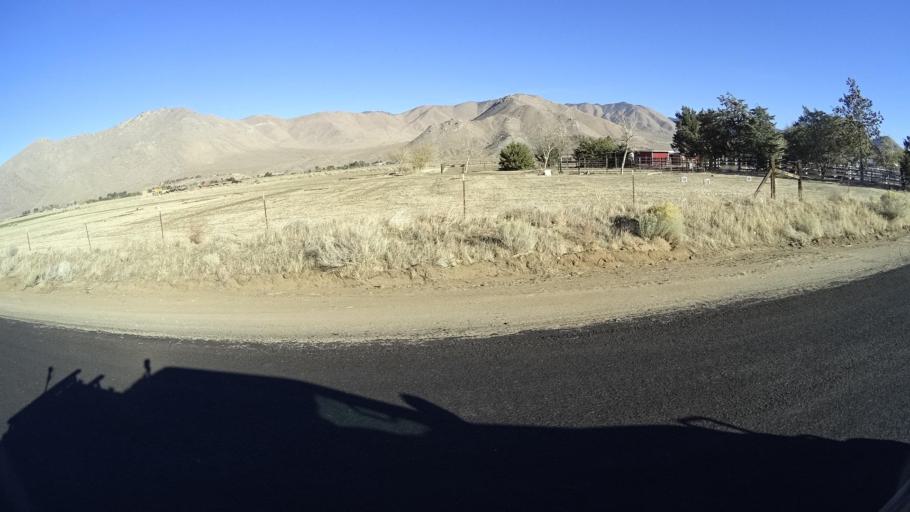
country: US
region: California
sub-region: Kern County
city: Weldon
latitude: 35.6271
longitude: -118.2645
